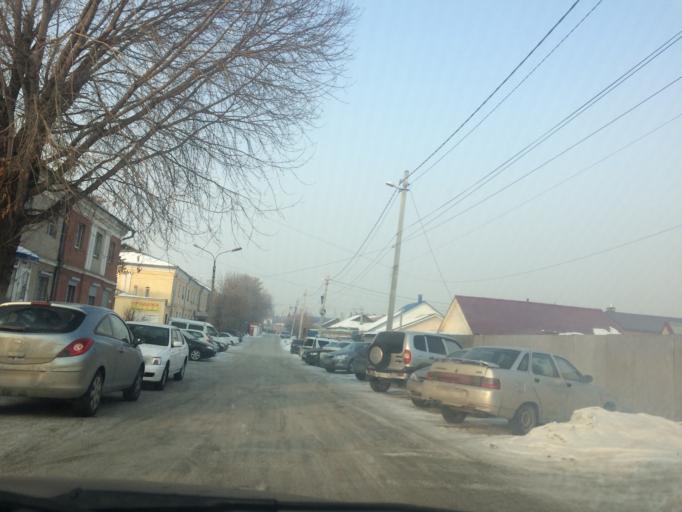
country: RU
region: Chelyabinsk
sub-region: Gorod Magnitogorsk
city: Magnitogorsk
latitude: 53.4196
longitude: 58.9641
